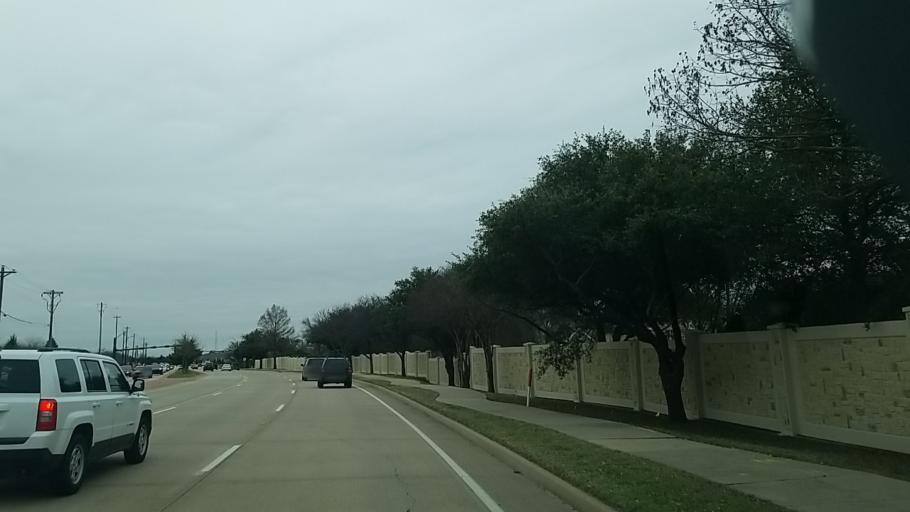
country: US
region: Texas
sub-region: Denton County
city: Flower Mound
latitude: 33.0050
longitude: -97.0710
